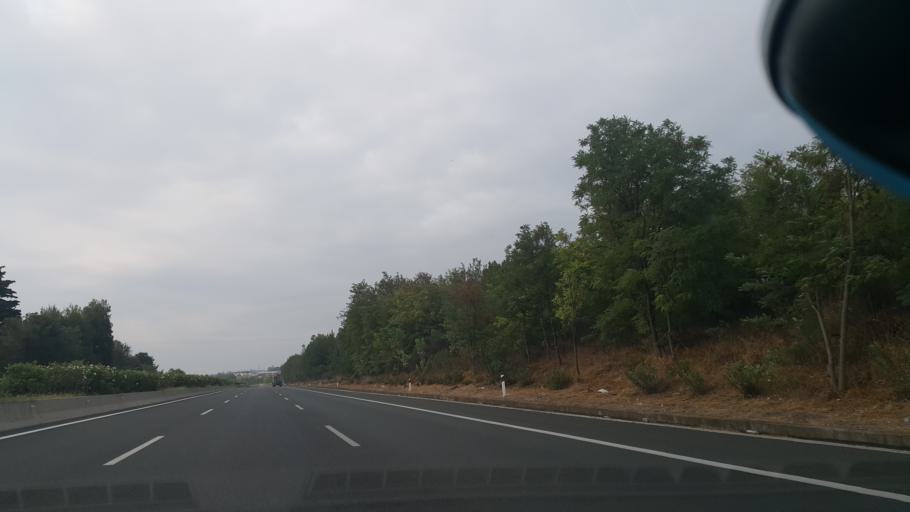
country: GR
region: Central Macedonia
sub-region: Nomos Pierias
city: Aiginio
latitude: 40.4784
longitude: 22.5694
